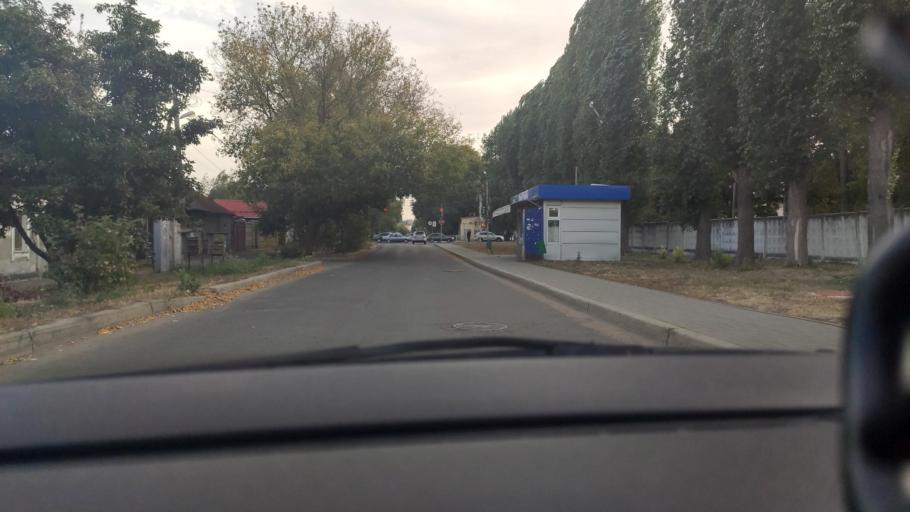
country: RU
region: Voronezj
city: Voronezh
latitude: 51.6940
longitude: 39.2141
